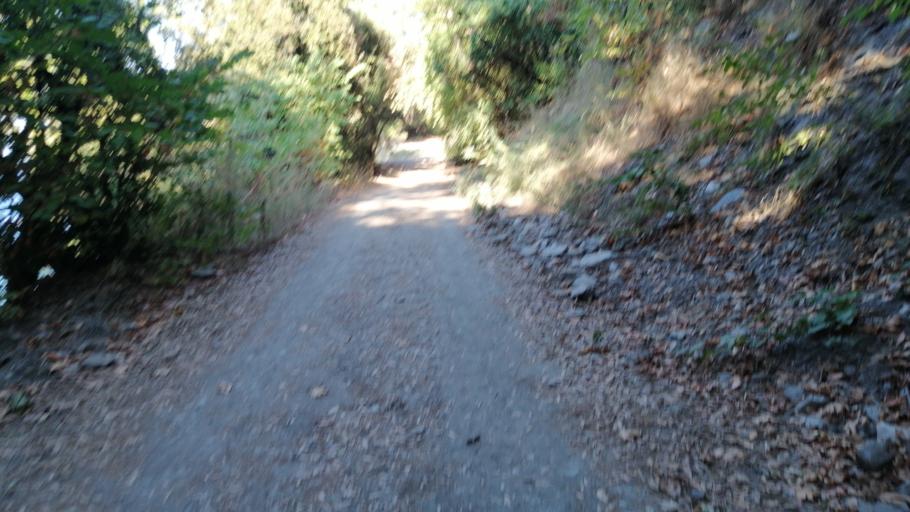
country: TR
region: Aydin
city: Atburgazi
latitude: 37.6901
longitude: 27.1352
